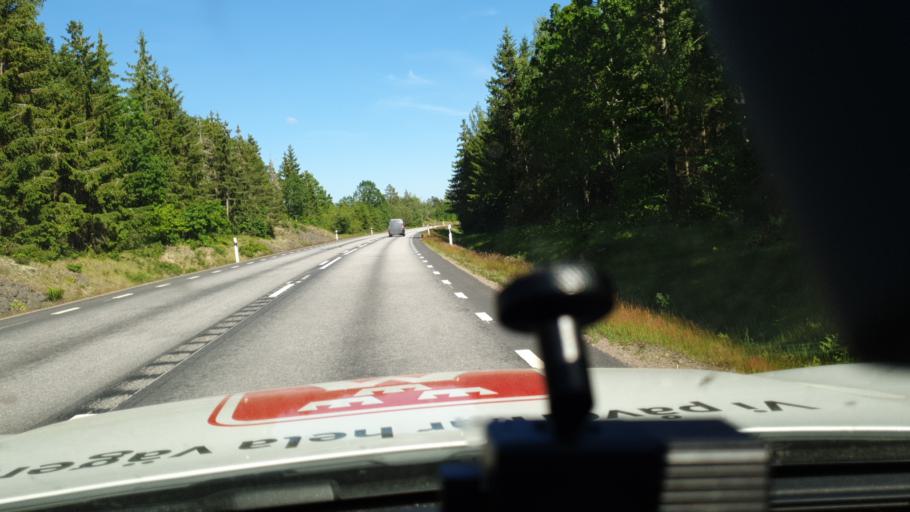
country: SE
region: Kalmar
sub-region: Vasterviks Kommun
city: Ankarsrum
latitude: 57.7079
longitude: 16.1405
